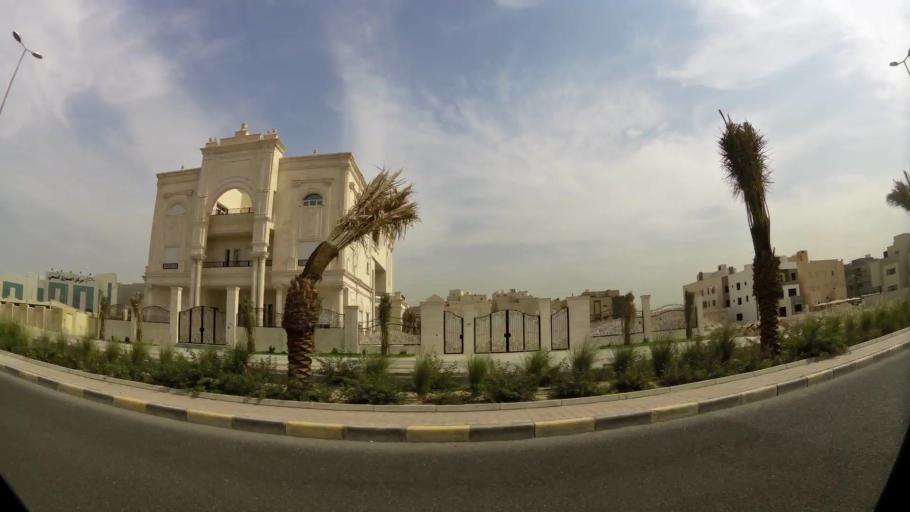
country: KW
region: Al Farwaniyah
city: Janub as Surrah
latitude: 29.2924
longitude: 47.9922
